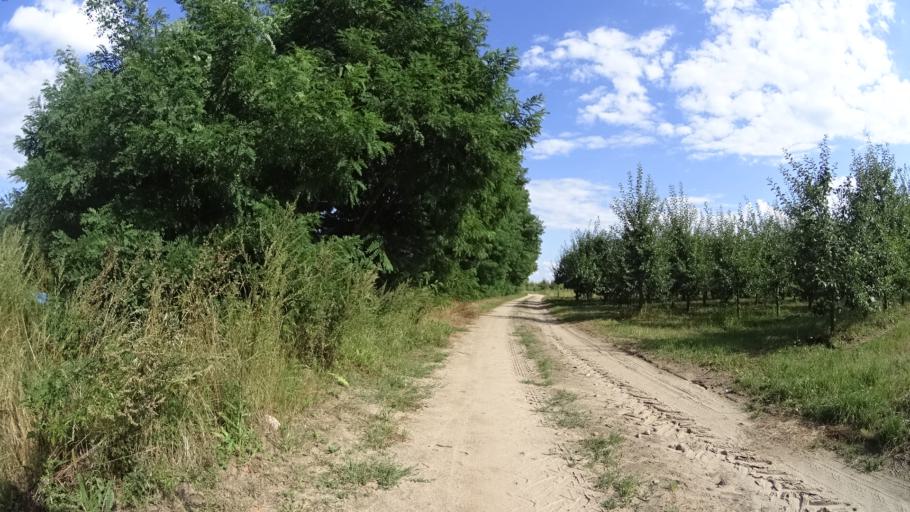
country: PL
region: Masovian Voivodeship
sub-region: Powiat bialobrzeski
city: Wysmierzyce
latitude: 51.6761
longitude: 20.7846
